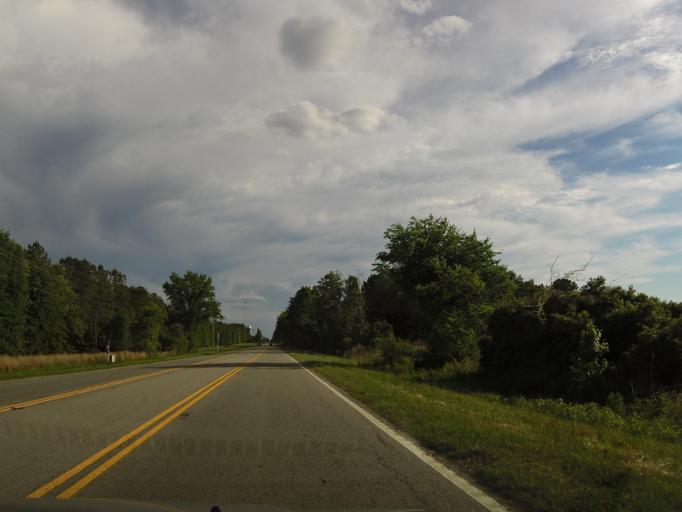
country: US
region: South Carolina
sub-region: Hampton County
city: Estill
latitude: 32.7885
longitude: -81.2406
